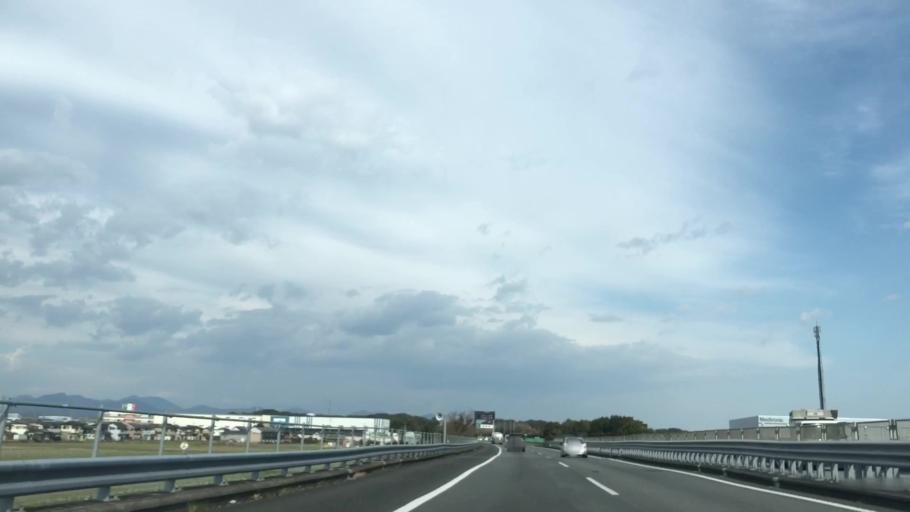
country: JP
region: Shizuoka
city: Fukuroi
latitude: 34.7562
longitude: 137.8933
